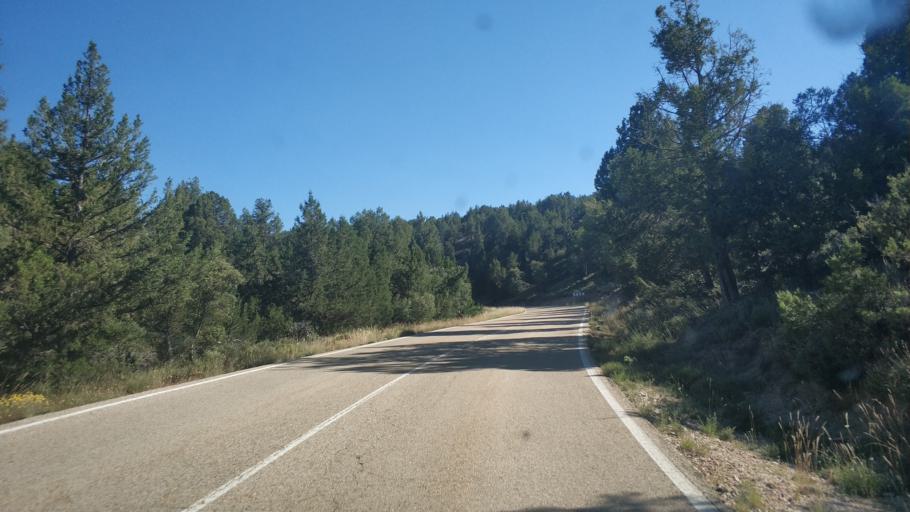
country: ES
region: Castille and Leon
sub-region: Provincia de Soria
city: Montejo de Tiermes
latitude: 41.4313
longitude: -3.2046
